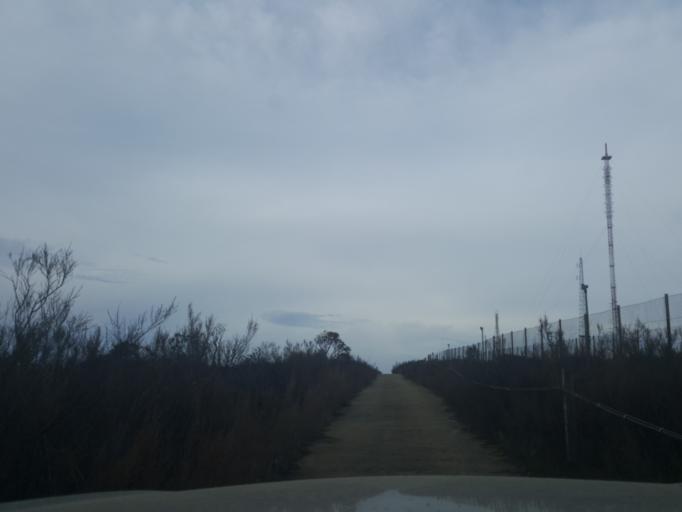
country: ZA
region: Limpopo
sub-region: Mopani District Municipality
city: Hoedspruit
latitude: -24.5456
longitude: 30.8654
